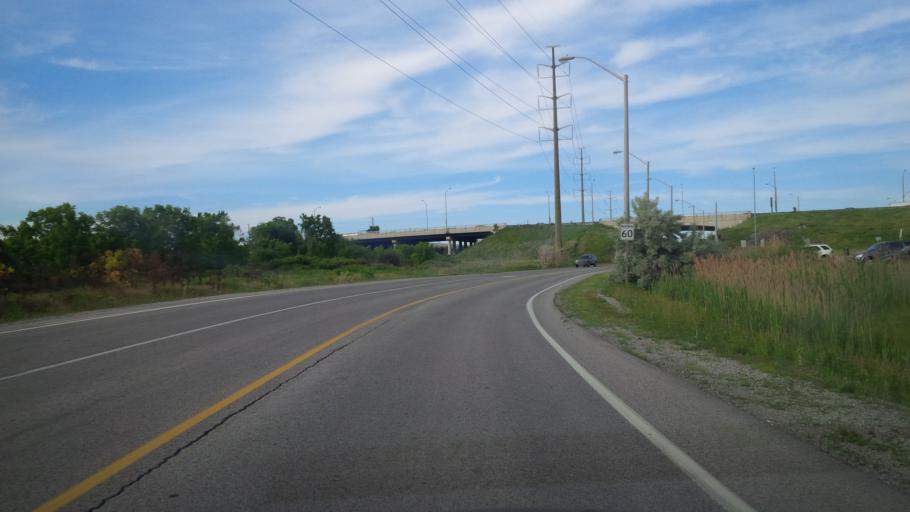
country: CA
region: Ontario
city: Burlington
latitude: 43.3520
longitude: -79.8078
